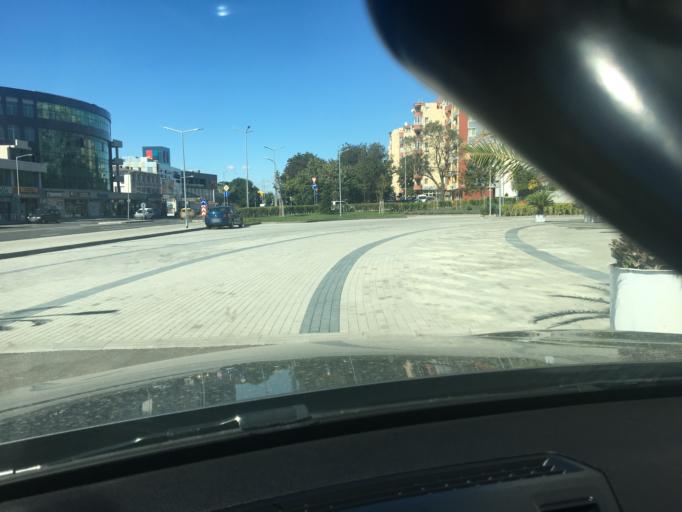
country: BG
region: Burgas
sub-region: Obshtina Burgas
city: Burgas
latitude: 42.5123
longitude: 27.4584
